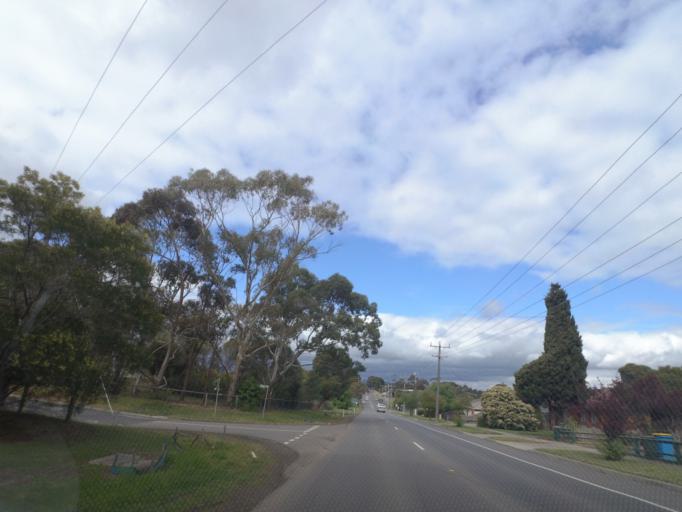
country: AU
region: Victoria
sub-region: Whittlesea
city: Whittlesea
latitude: -37.4063
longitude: 144.9767
